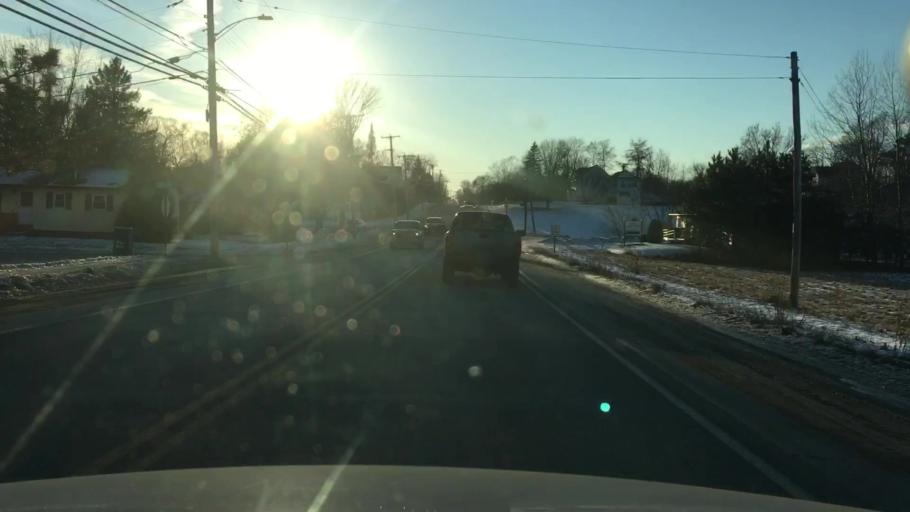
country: US
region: Maine
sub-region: Penobscot County
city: Brewer
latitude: 44.8025
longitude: -68.7491
